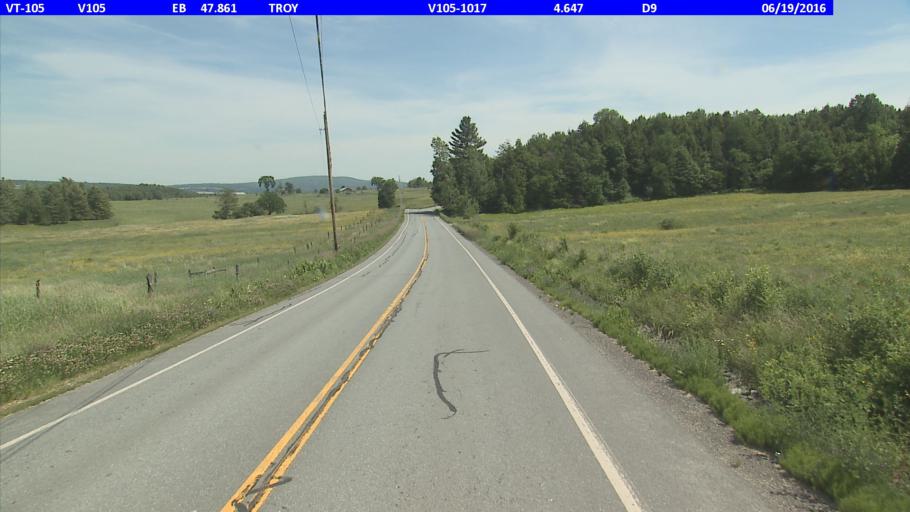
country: US
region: Vermont
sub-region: Orleans County
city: Newport
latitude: 44.9882
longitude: -72.3659
